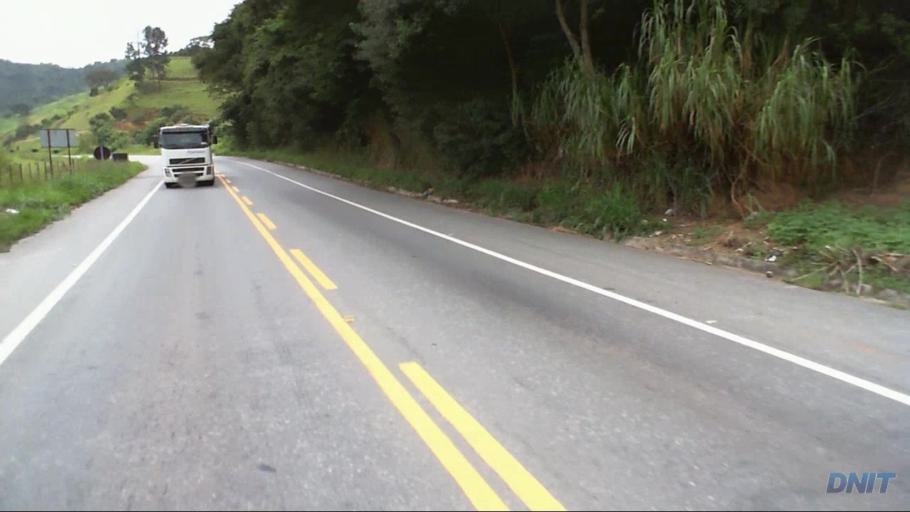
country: BR
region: Minas Gerais
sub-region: Nova Era
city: Nova Era
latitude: -19.7207
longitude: -43.0055
